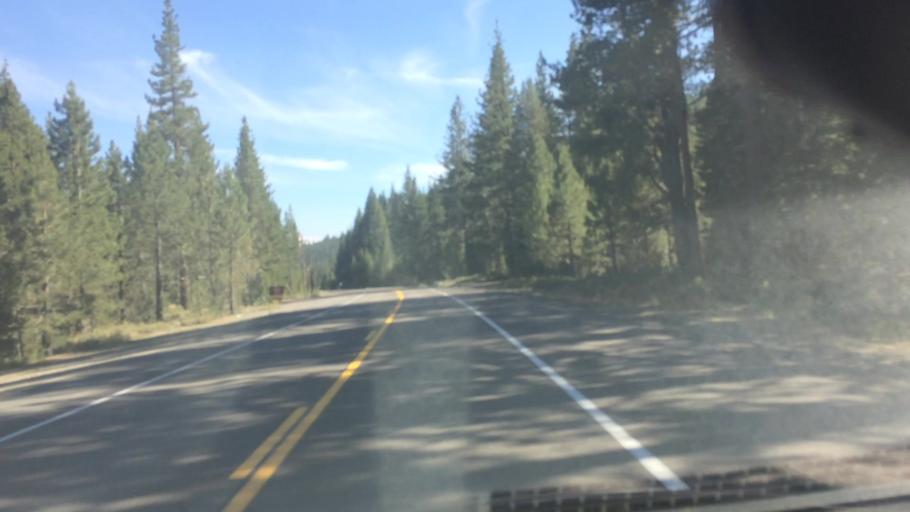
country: US
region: California
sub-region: Nevada County
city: Truckee
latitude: 39.2597
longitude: -120.2116
